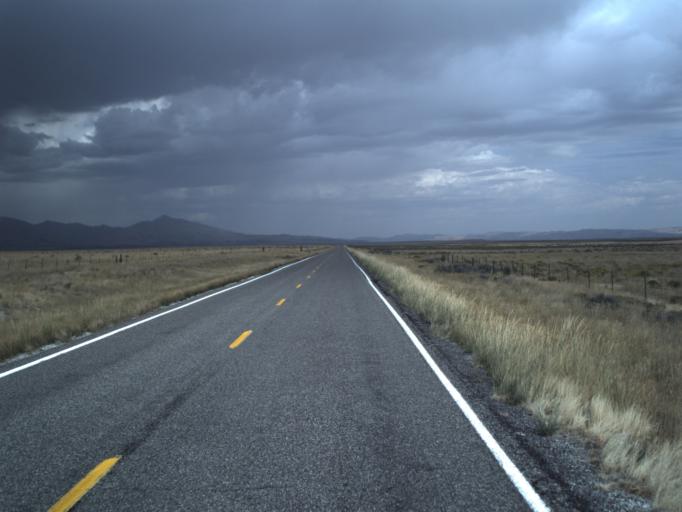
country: US
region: Idaho
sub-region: Oneida County
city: Malad City
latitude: 41.8886
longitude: -113.1131
